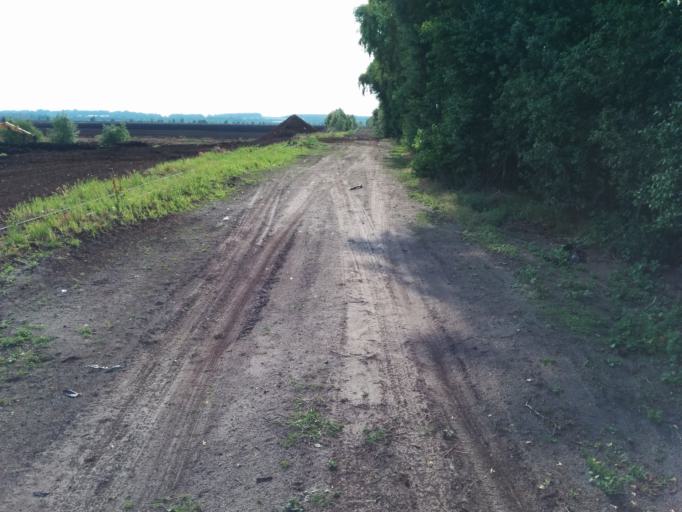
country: DE
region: Lower Saxony
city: Diepholz
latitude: 52.6446
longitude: 8.3086
